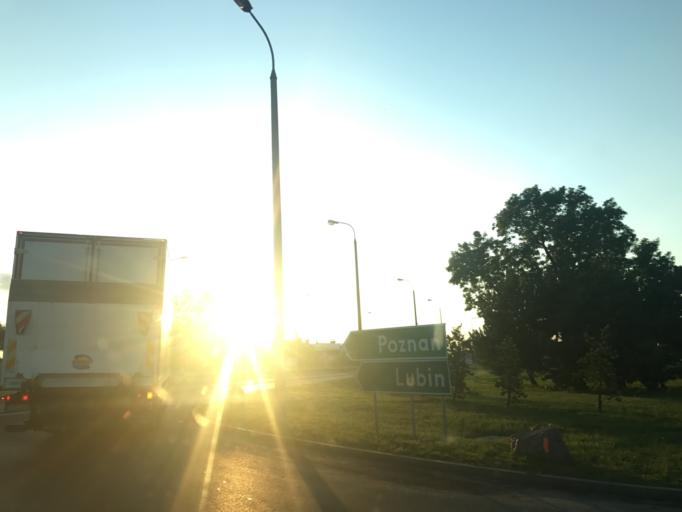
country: PL
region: Greater Poland Voivodeship
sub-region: Powiat rawicki
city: Rawicz
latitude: 51.6177
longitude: 16.8598
